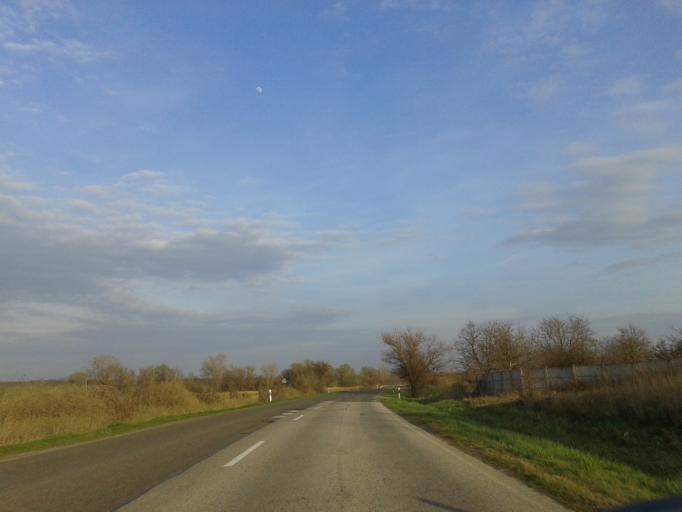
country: HU
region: Komarom-Esztergom
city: Acs
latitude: 47.7265
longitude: 18.0071
